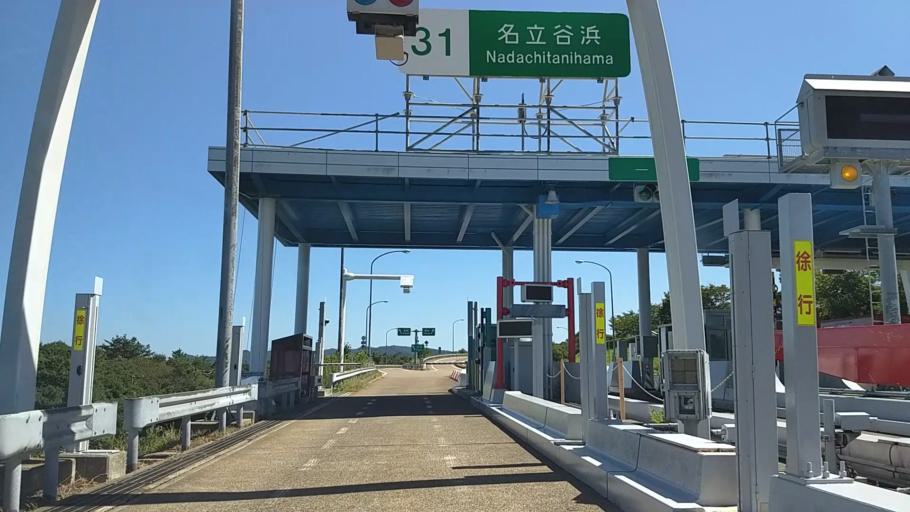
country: JP
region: Niigata
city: Joetsu
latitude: 37.1688
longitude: 138.1111
